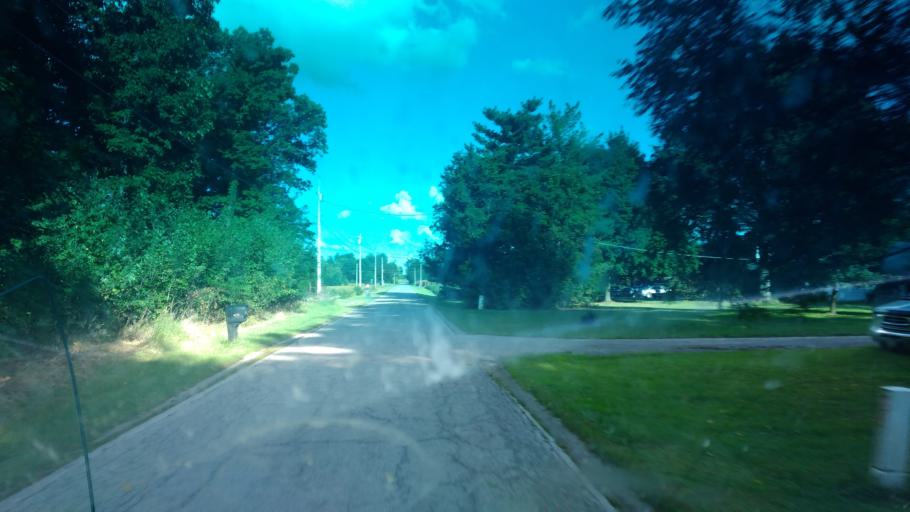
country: US
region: Ohio
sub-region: Hancock County
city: Arlington
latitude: 40.9360
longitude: -83.6773
